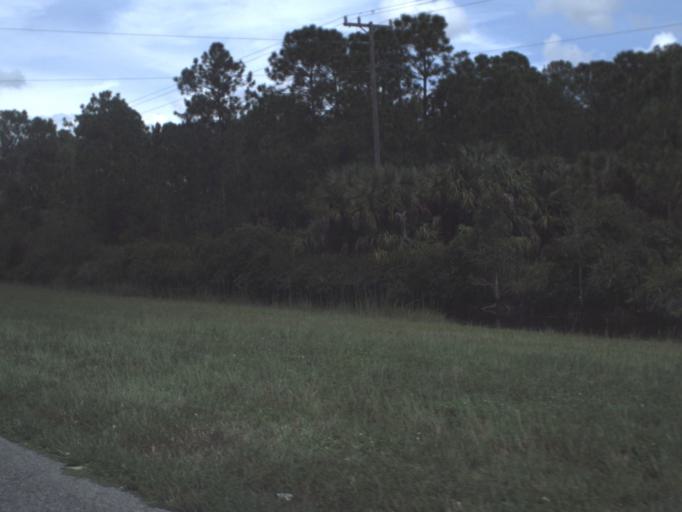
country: US
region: Florida
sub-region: Charlotte County
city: Charlotte Park
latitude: 26.8419
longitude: -81.9773
